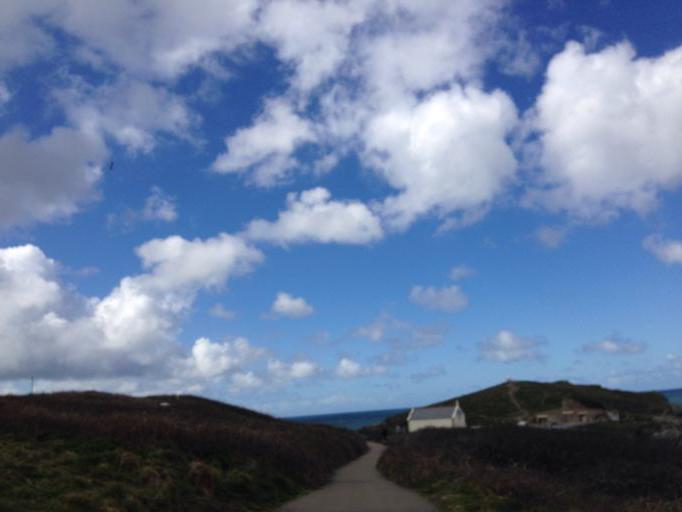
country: GB
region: England
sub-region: Cornwall
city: Newquay
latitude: 50.4216
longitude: -5.0958
